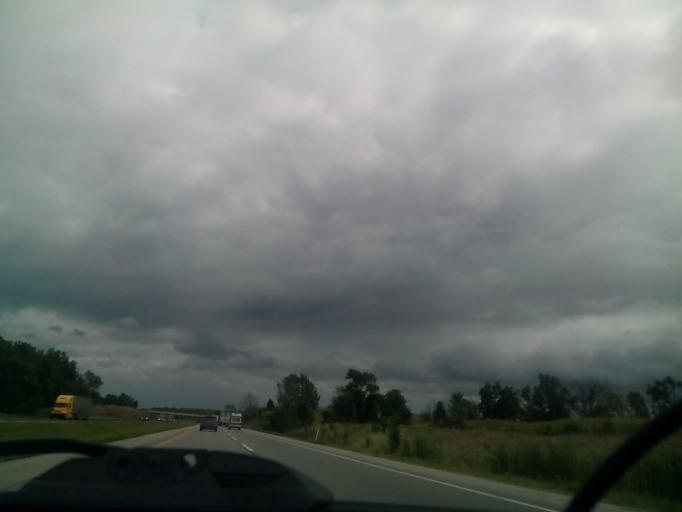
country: US
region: Indiana
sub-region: Steuben County
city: Fremont
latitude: 41.6777
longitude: -84.8739
